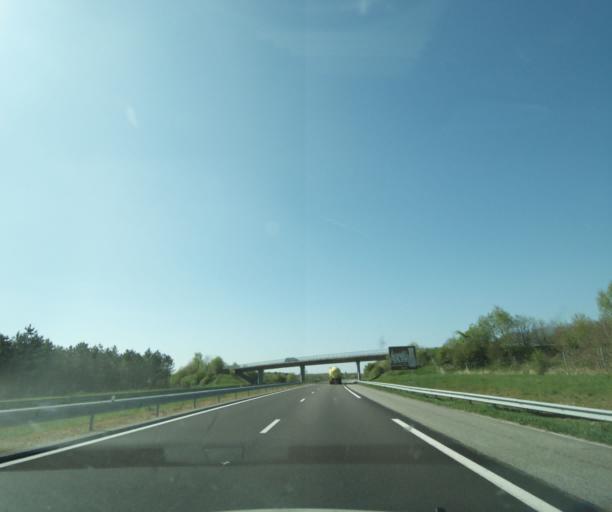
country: FR
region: Centre
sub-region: Departement du Loiret
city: Ouzouer-sur-Trezee
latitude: 47.6201
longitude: 2.8014
